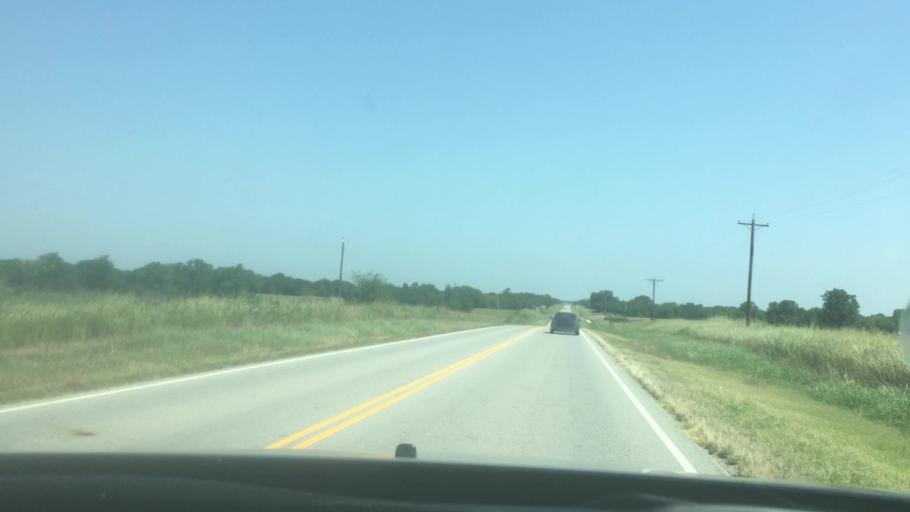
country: US
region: Oklahoma
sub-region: Coal County
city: Coalgate
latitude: 34.4410
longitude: -96.4245
